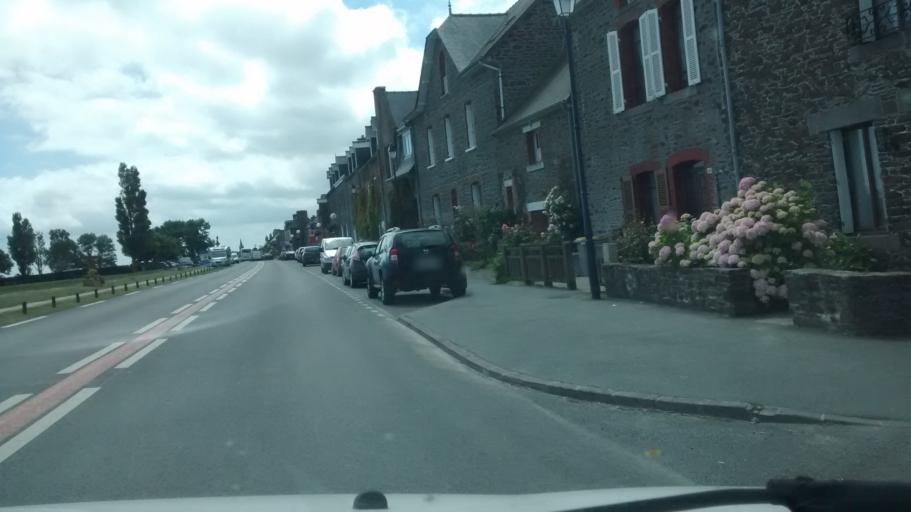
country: FR
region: Brittany
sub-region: Departement d'Ille-et-Vilaine
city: La Fresnais
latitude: 48.6208
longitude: -1.8527
